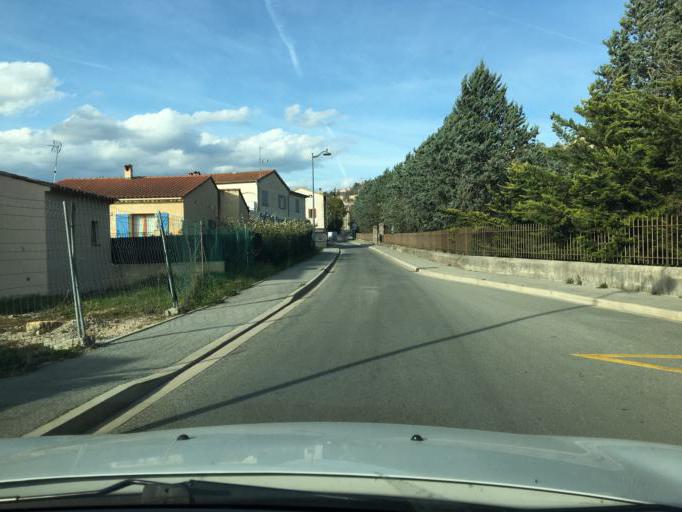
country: FR
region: Provence-Alpes-Cote d'Azur
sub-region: Departement du Var
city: Fayence
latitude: 43.6198
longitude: 6.6900
